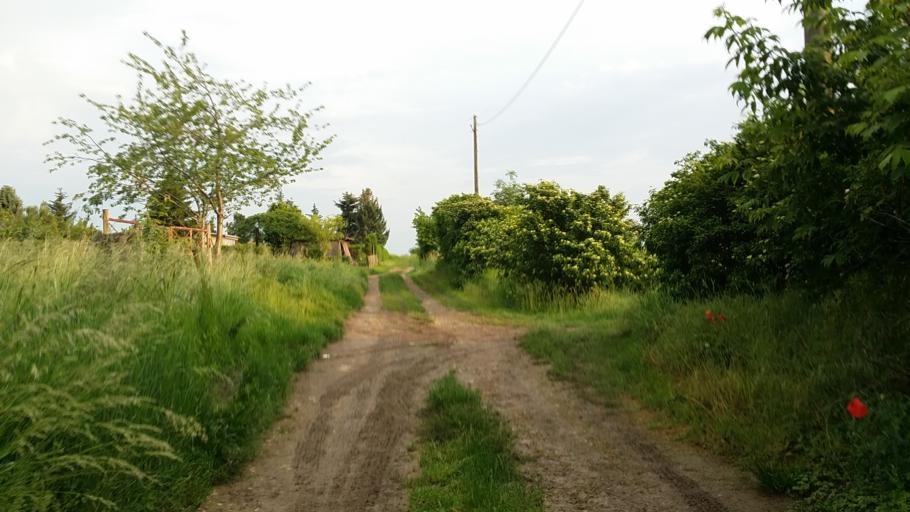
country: DE
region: Thuringia
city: Erfurt
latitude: 50.9634
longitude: 11.0798
